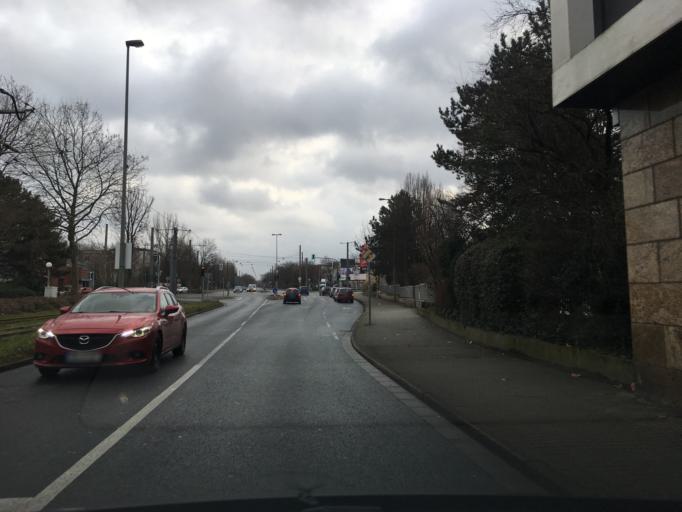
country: DE
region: North Rhine-Westphalia
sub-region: Regierungsbezirk Dusseldorf
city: Oberhausen
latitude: 51.4709
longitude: 6.8624
